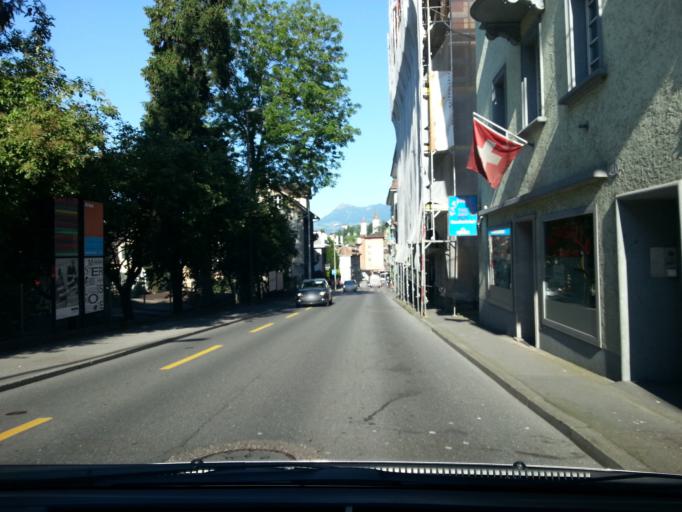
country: CH
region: Lucerne
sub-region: Lucerne-Stadt District
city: Luzern
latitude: 47.0543
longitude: 8.2884
